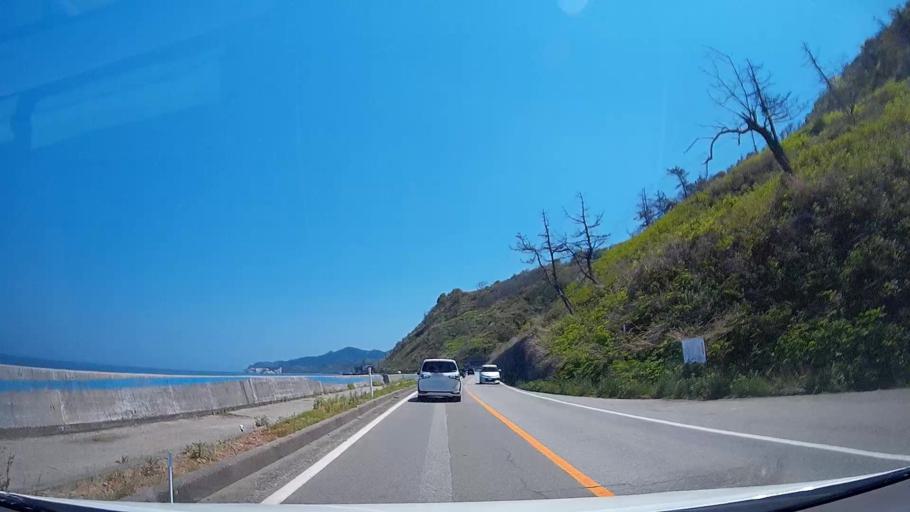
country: JP
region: Ishikawa
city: Nanao
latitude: 37.4307
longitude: 137.0109
